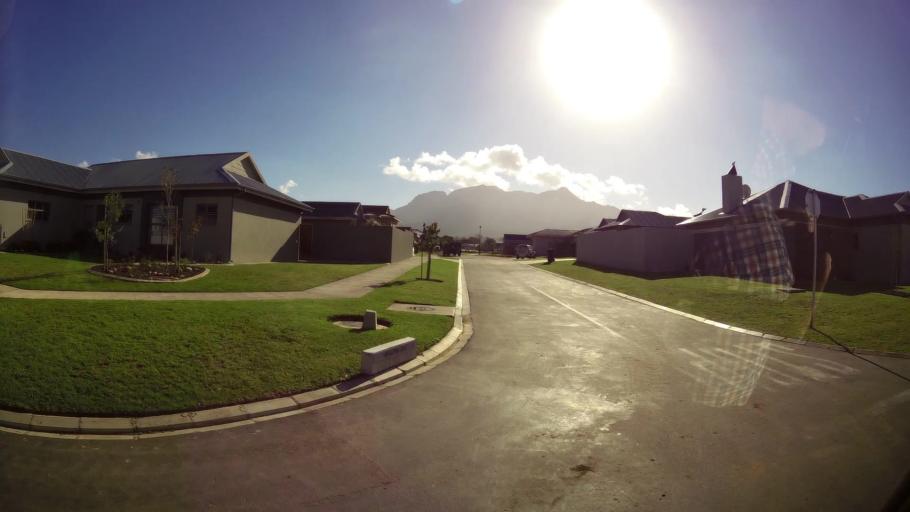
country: ZA
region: Western Cape
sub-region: Eden District Municipality
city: George
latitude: -33.9614
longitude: 22.4206
